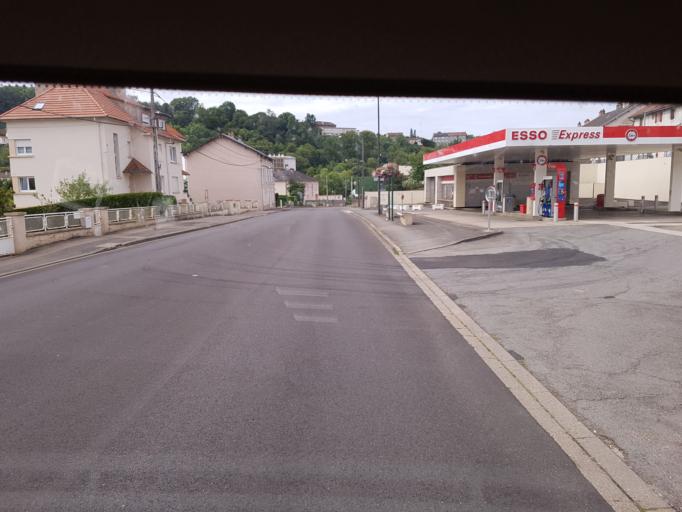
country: FR
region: Lorraine
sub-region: Departement de Meurthe-et-Moselle
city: Joeuf
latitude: 49.2252
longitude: 6.0147
